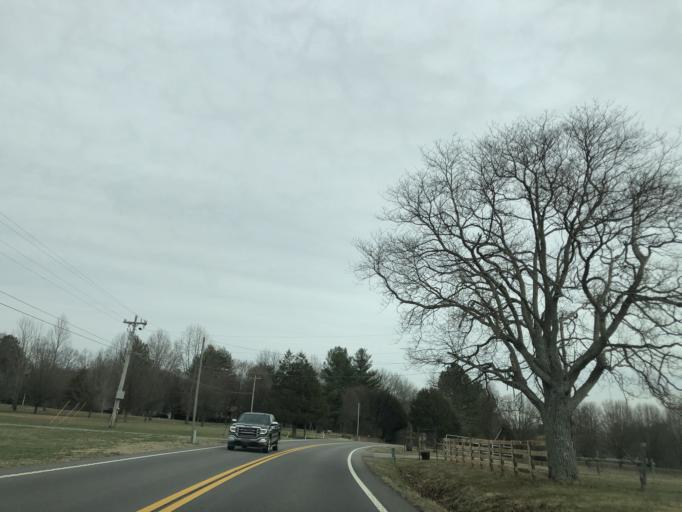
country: US
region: Tennessee
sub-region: Robertson County
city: Greenbrier
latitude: 36.4812
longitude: -86.7824
